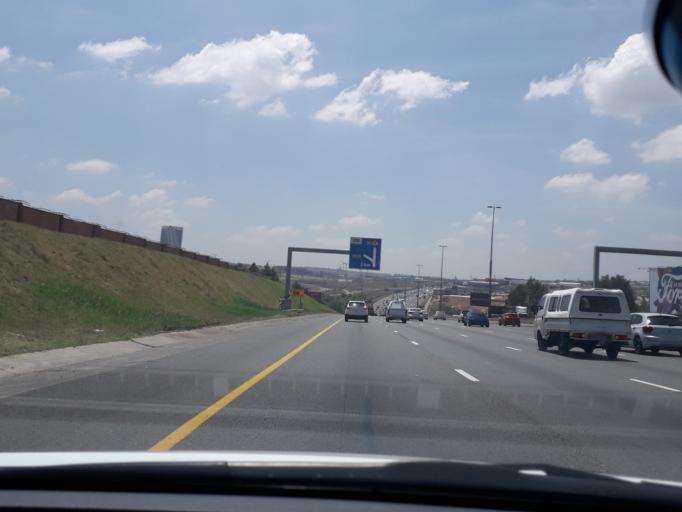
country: ZA
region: Gauteng
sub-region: City of Johannesburg Metropolitan Municipality
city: Midrand
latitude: -26.0363
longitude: 28.1072
